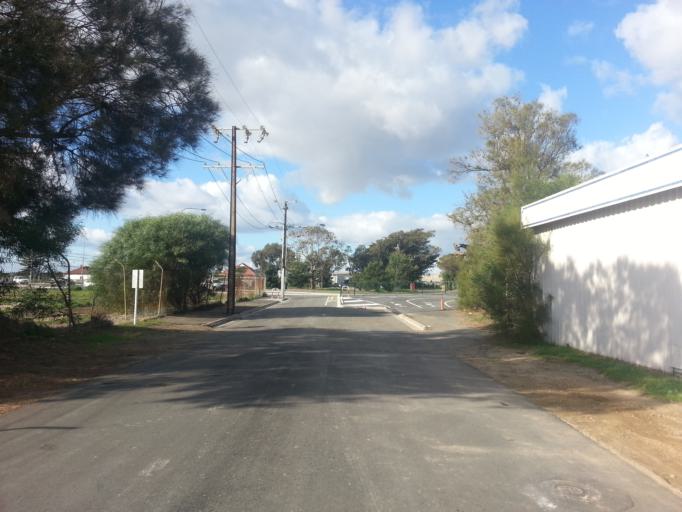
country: AU
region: South Australia
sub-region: Port Adelaide Enfield
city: Birkenhead
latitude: -34.8403
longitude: 138.5008
